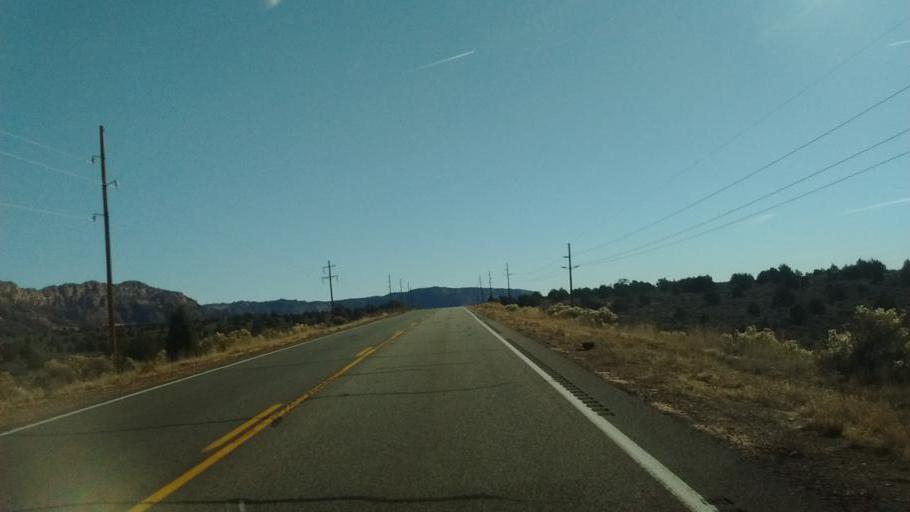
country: US
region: Arizona
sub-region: Mohave County
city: Colorado City
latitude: 37.0225
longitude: -113.0399
